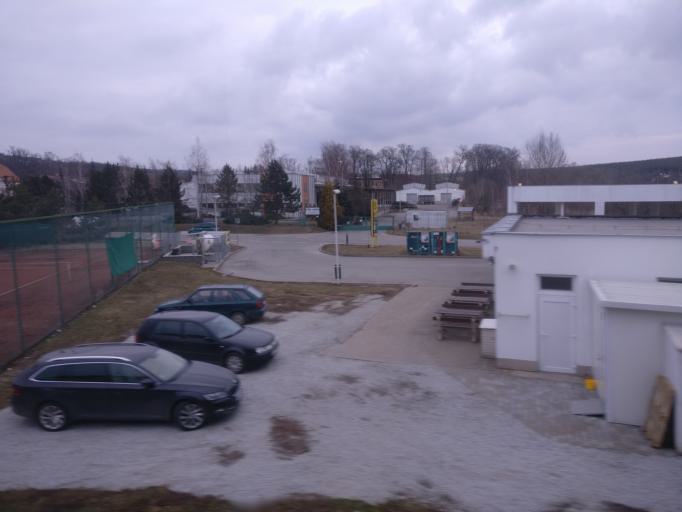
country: CZ
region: South Moravian
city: Zastavka
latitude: 49.1847
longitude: 16.3678
